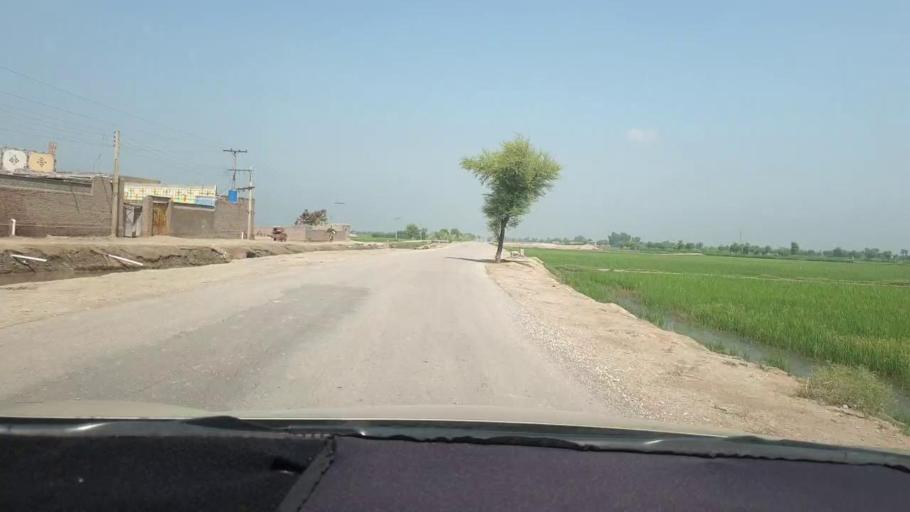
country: PK
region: Sindh
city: Miro Khan
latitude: 27.7732
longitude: 68.0588
